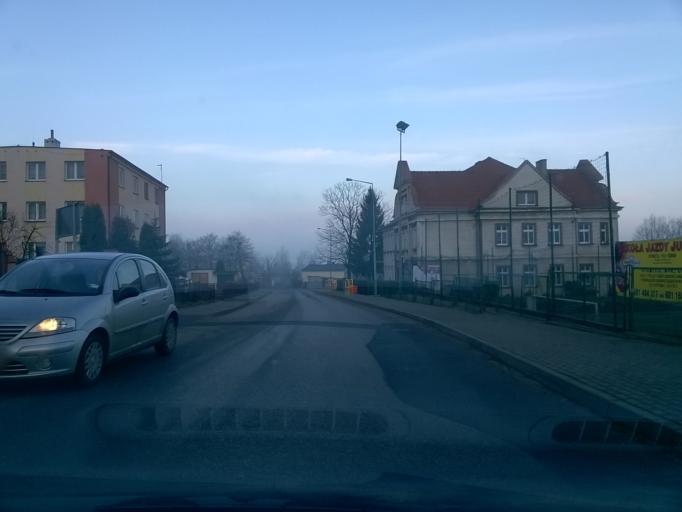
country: PL
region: Kujawsko-Pomorskie
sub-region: Powiat nakielski
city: Kcynia
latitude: 52.9935
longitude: 17.4938
